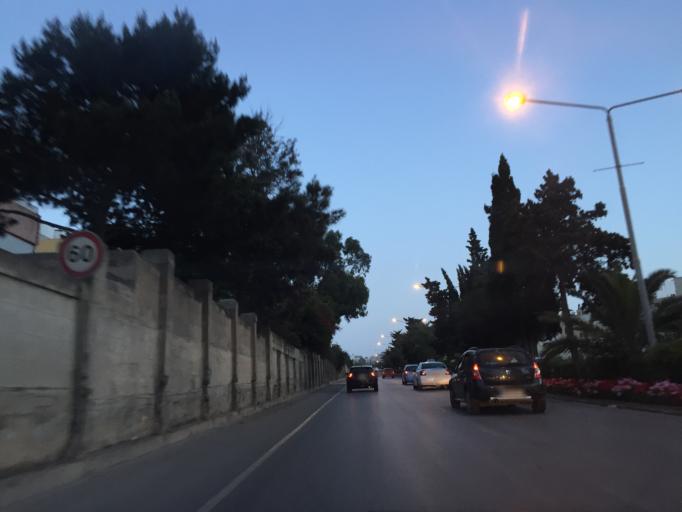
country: MT
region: Saint Julian
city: San Giljan
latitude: 35.9210
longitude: 14.4868
